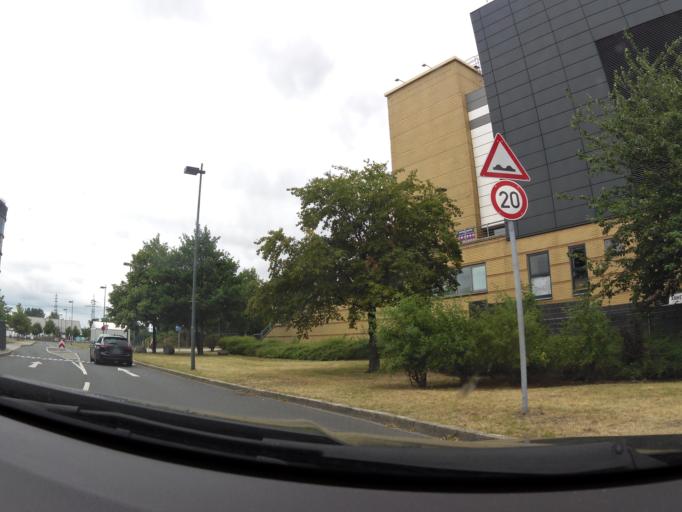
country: DE
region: North Rhine-Westphalia
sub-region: Regierungsbezirk Dusseldorf
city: Oberhausen
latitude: 51.4907
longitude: 6.8712
